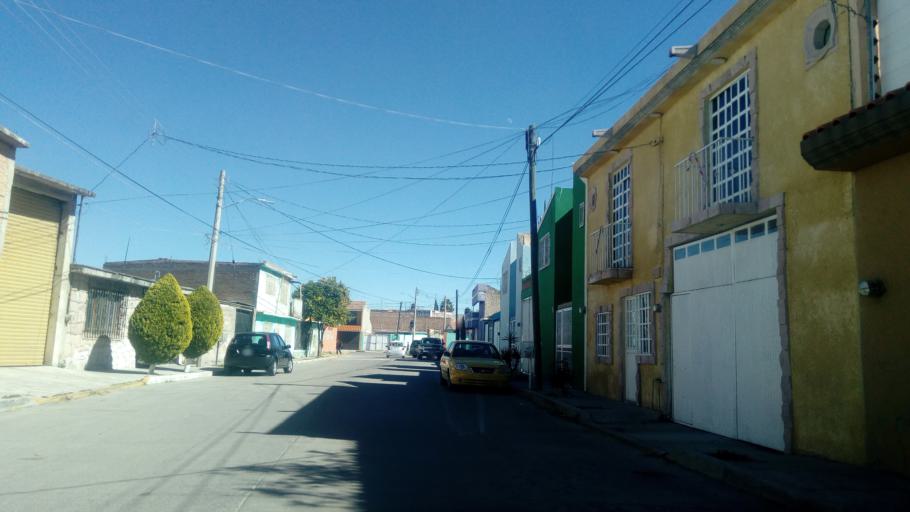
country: MX
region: Durango
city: Victoria de Durango
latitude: 24.0167
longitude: -104.6417
